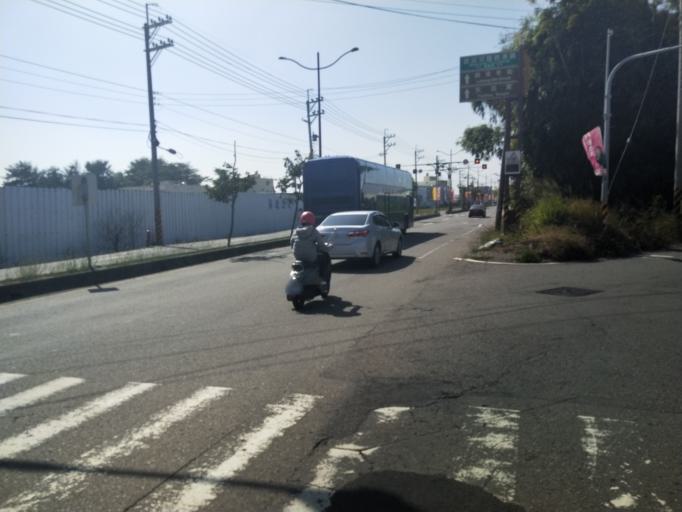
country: TW
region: Taiwan
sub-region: Changhua
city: Chang-hua
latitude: 24.0485
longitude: 120.4719
